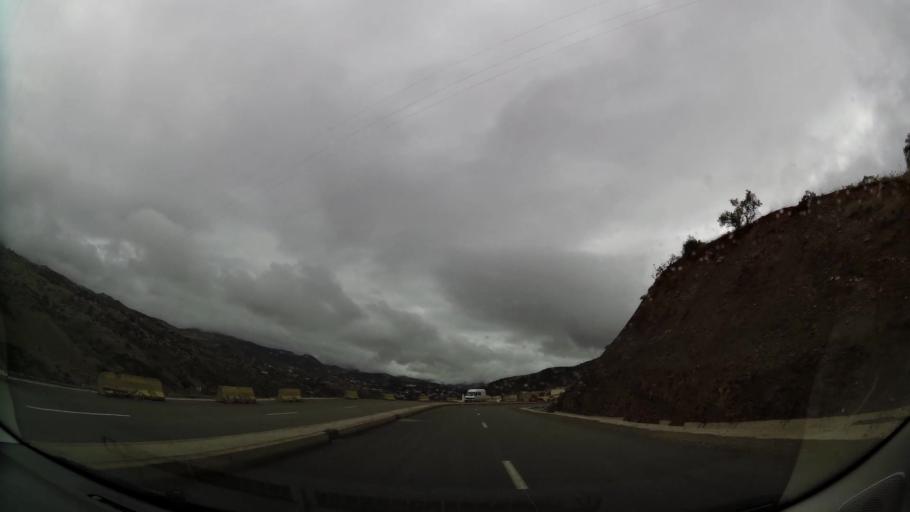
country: MA
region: Taza-Al Hoceima-Taounate
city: Imzourene
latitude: 34.9750
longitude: -3.8126
